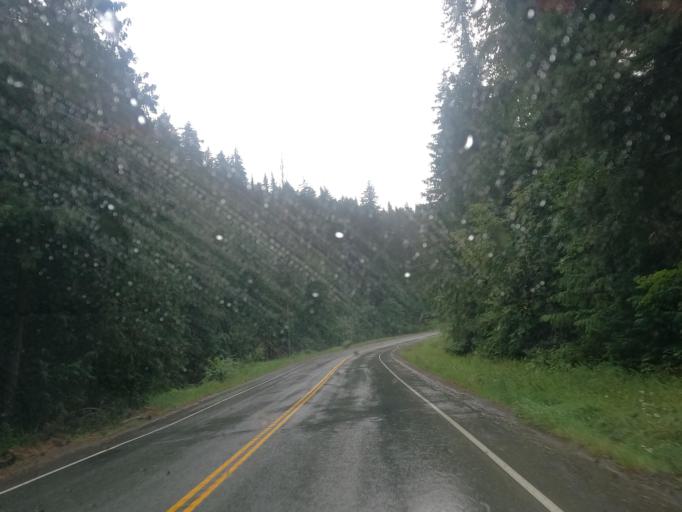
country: CA
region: British Columbia
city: Lillooet
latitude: 50.5343
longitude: -122.1465
